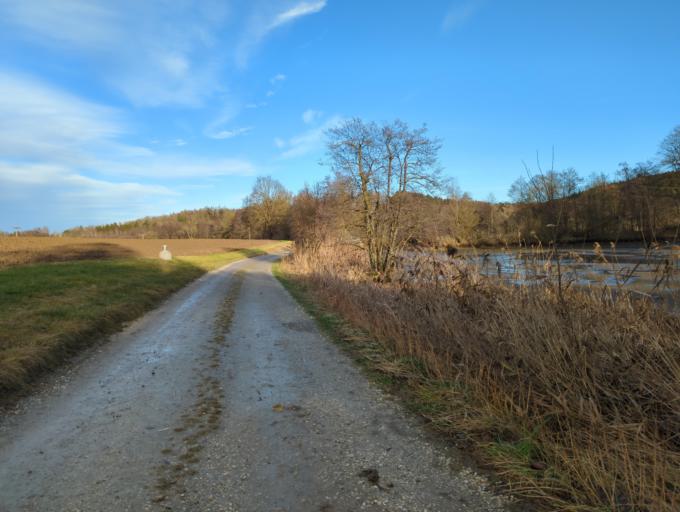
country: DE
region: Bavaria
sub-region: Swabia
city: Roggenburg
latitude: 48.2787
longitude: 10.2131
